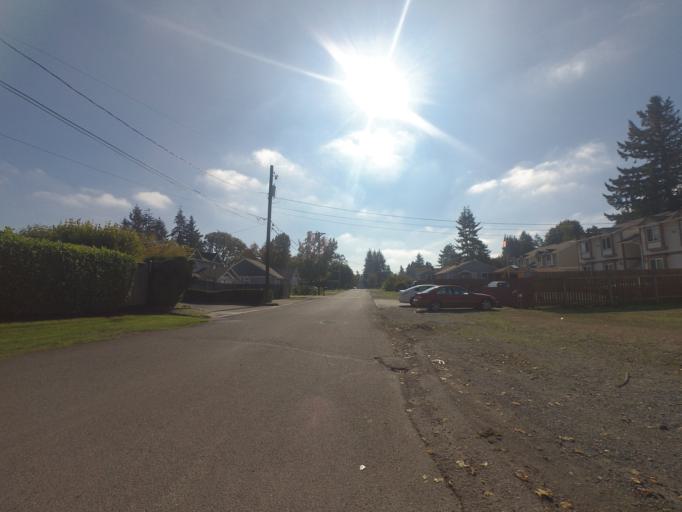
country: US
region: Washington
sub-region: Pierce County
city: Lakewood
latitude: 47.1893
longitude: -122.5112
